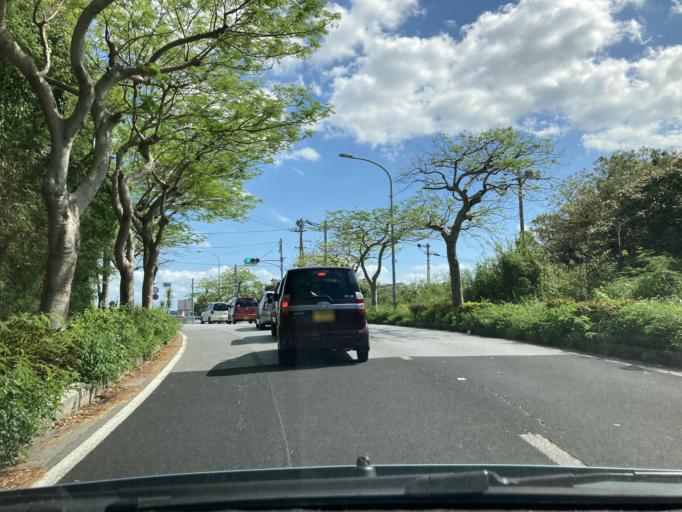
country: JP
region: Okinawa
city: Tomigusuku
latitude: 26.1974
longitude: 127.7004
